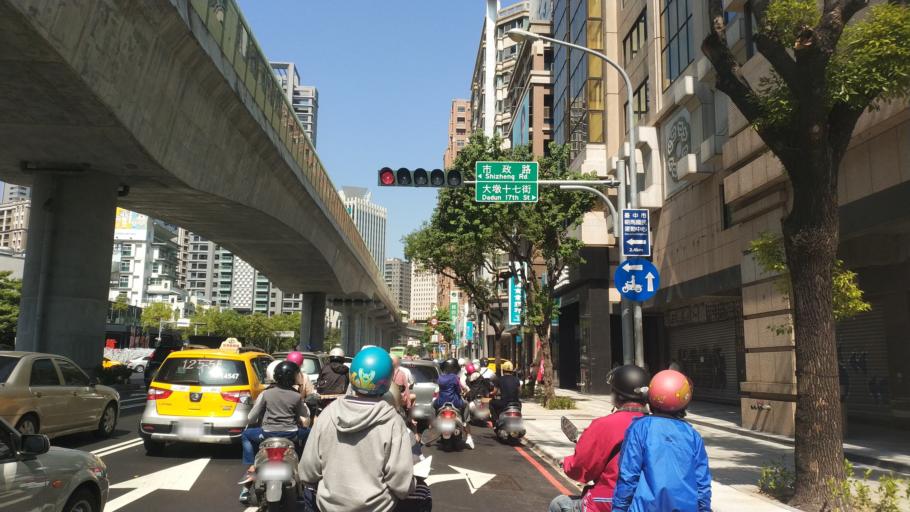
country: TW
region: Taiwan
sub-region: Taichung City
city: Taichung
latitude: 24.1551
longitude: 120.6469
